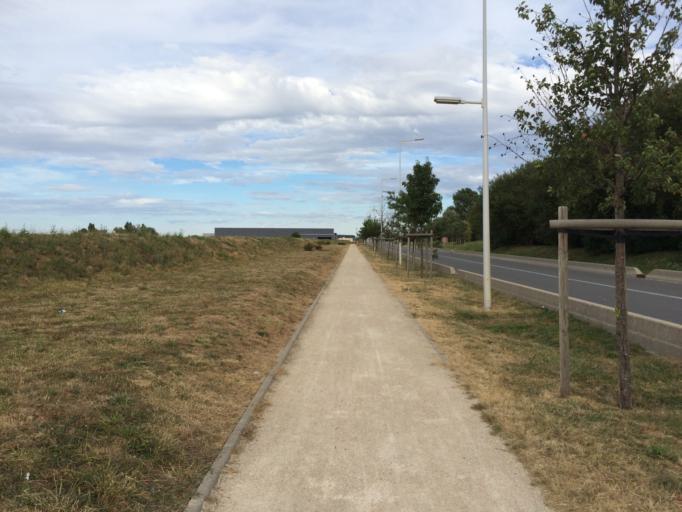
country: FR
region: Ile-de-France
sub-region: Departement de l'Essonne
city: Chilly-Mazarin
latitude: 48.7181
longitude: 2.3244
